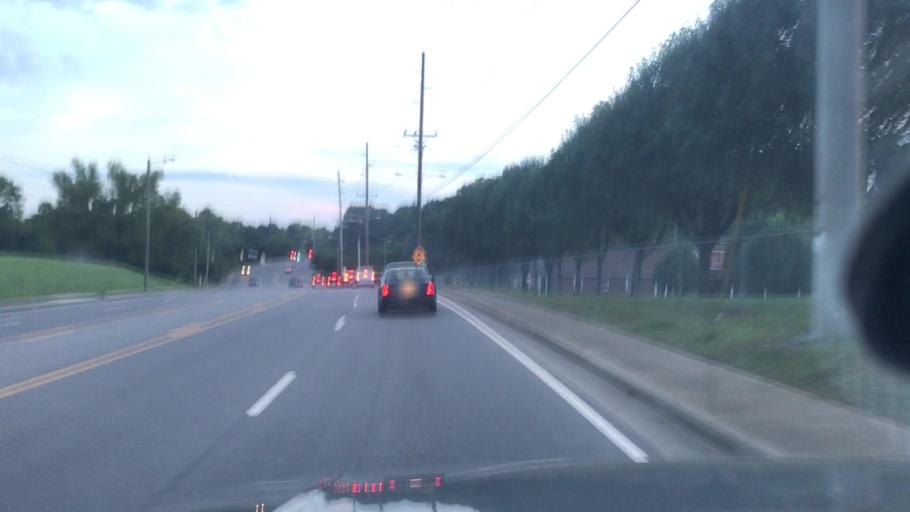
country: US
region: Tennessee
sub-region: Davidson County
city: Nashville
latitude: 36.2036
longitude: -86.8194
